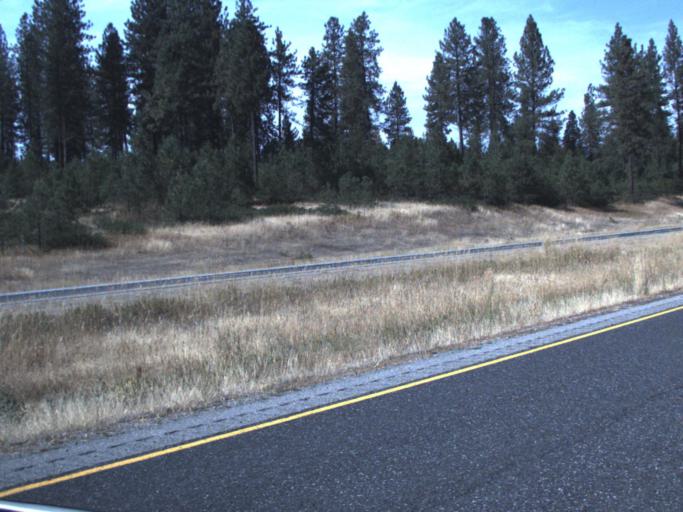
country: US
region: Washington
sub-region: Spokane County
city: Deer Park
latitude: 47.9071
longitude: -117.3506
